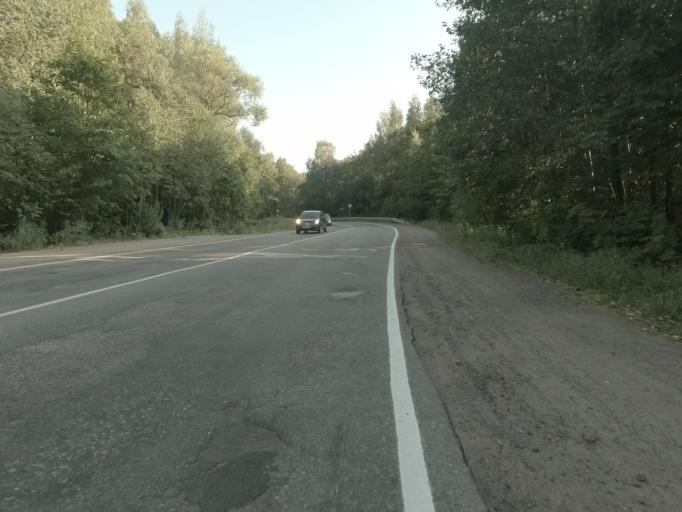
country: RU
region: Leningrad
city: Vyborg
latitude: 60.7288
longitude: 28.7599
